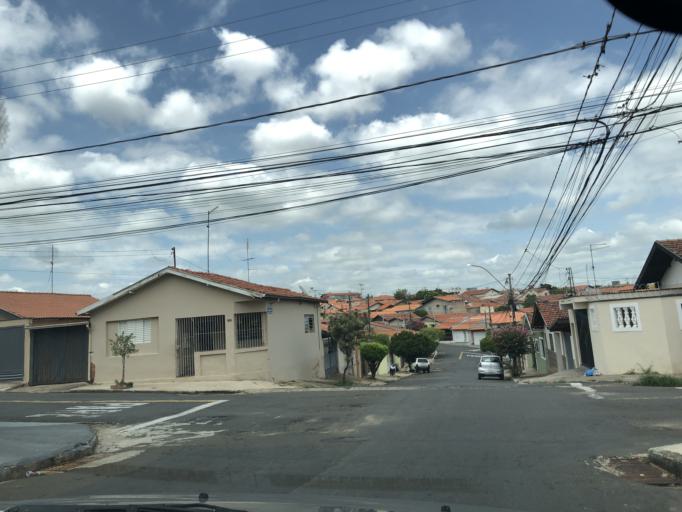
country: BR
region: Sao Paulo
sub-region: Piracicaba
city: Piracicaba
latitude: -22.7492
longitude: -47.6505
